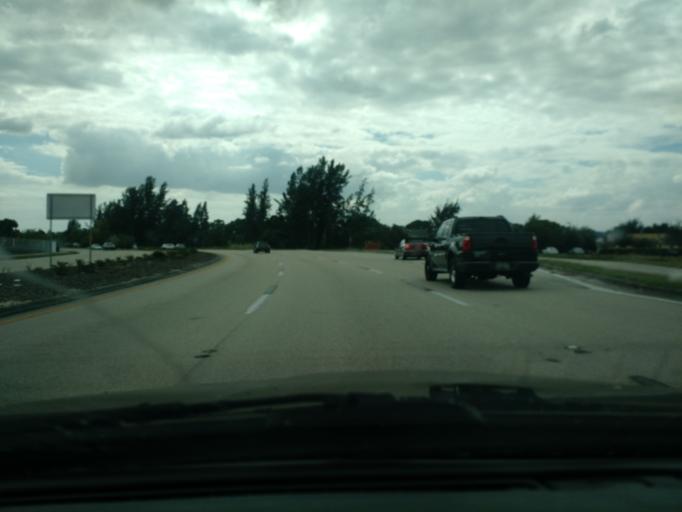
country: US
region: Florida
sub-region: Lee County
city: Pine Manor
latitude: 26.5923
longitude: -81.8686
